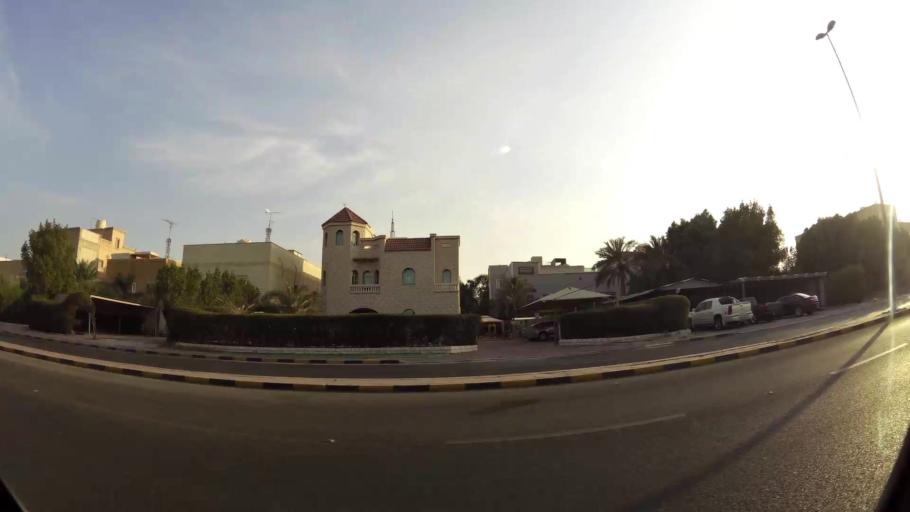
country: KW
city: Al Funaytis
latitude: 29.2212
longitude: 48.0715
